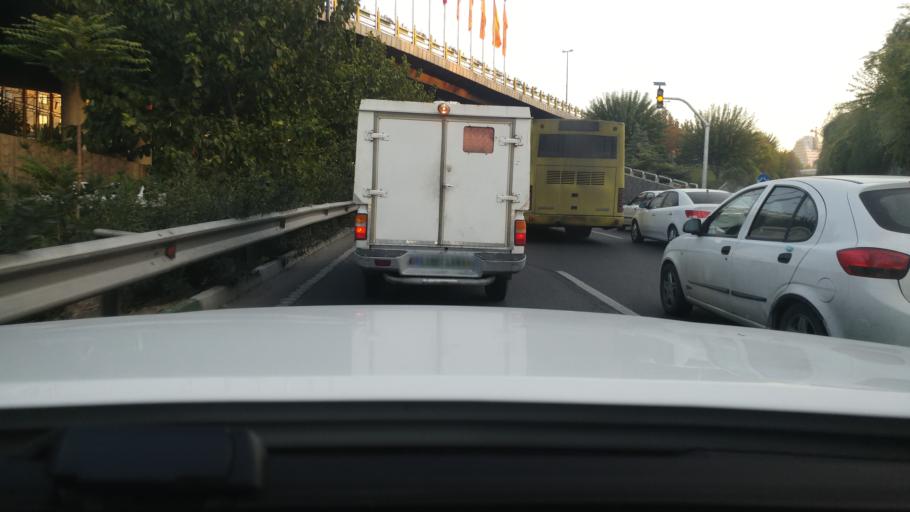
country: IR
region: Tehran
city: Tehran
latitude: 35.7341
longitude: 51.3118
